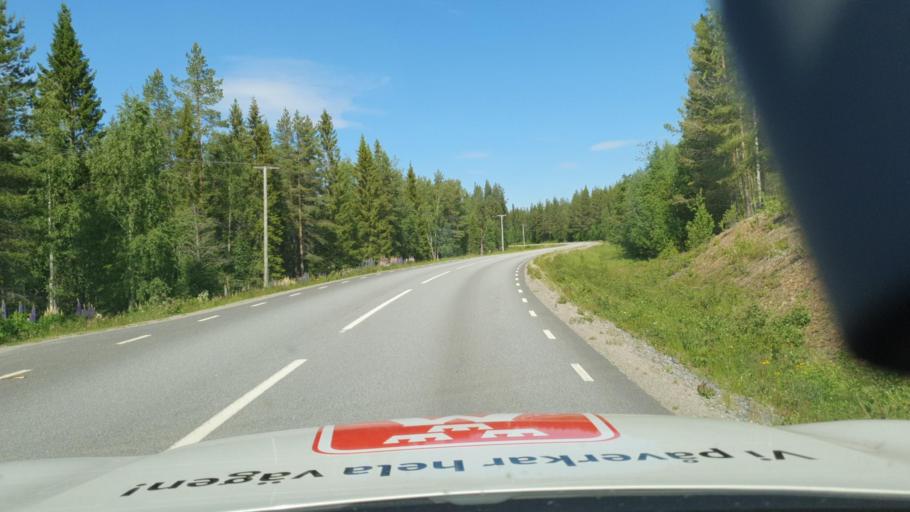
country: SE
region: Vaesterbotten
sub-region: Skelleftea Kommun
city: Langsele
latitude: 64.7475
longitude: 20.3498
